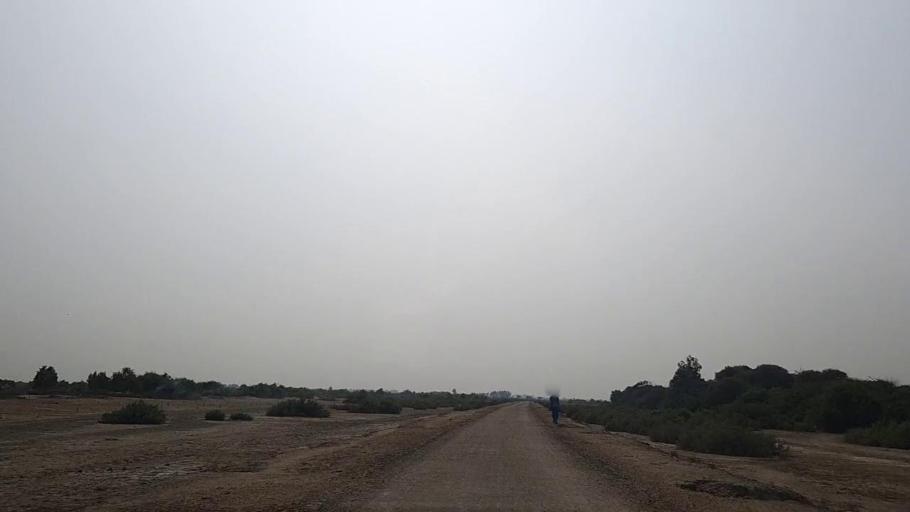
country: PK
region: Sindh
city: Mirpur Sakro
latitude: 24.6465
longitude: 67.7675
